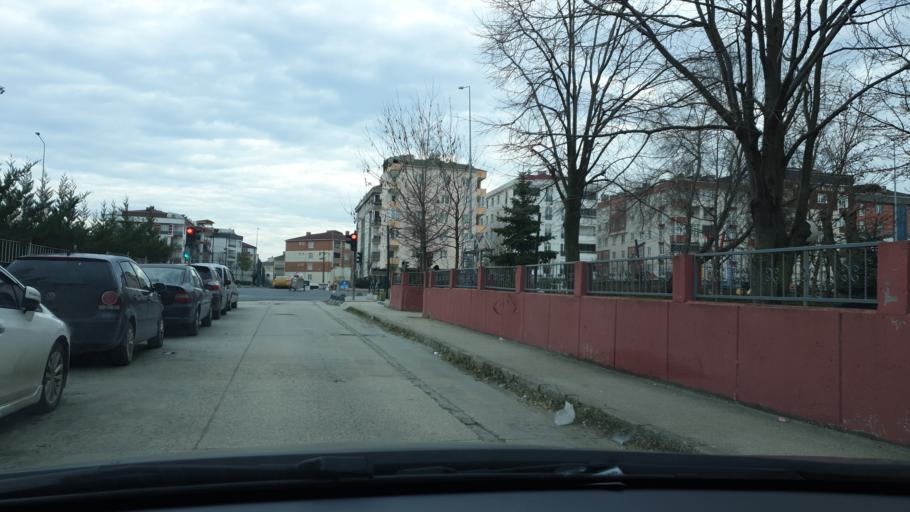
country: TR
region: Tekirdag
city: Cerkezkoey
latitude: 41.2820
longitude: 27.9824
